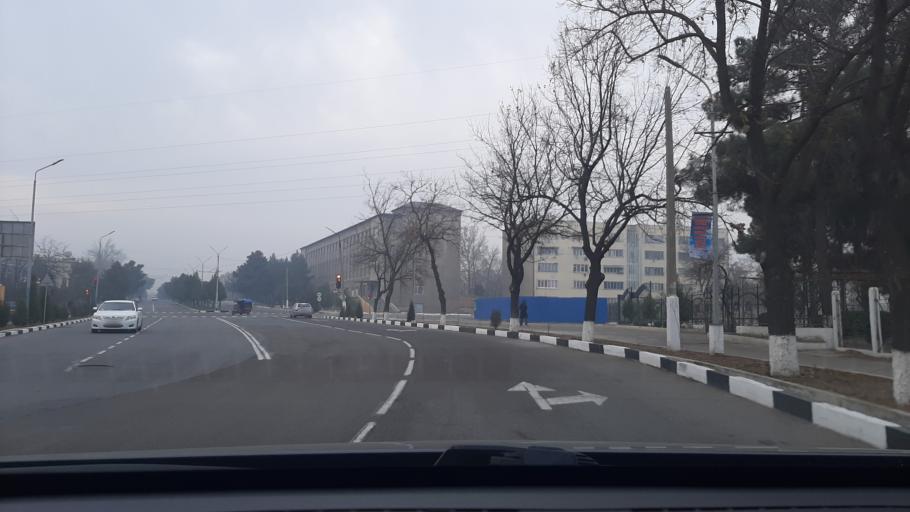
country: TJ
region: Viloyati Sughd
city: Chkalov
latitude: 40.2360
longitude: 69.6883
